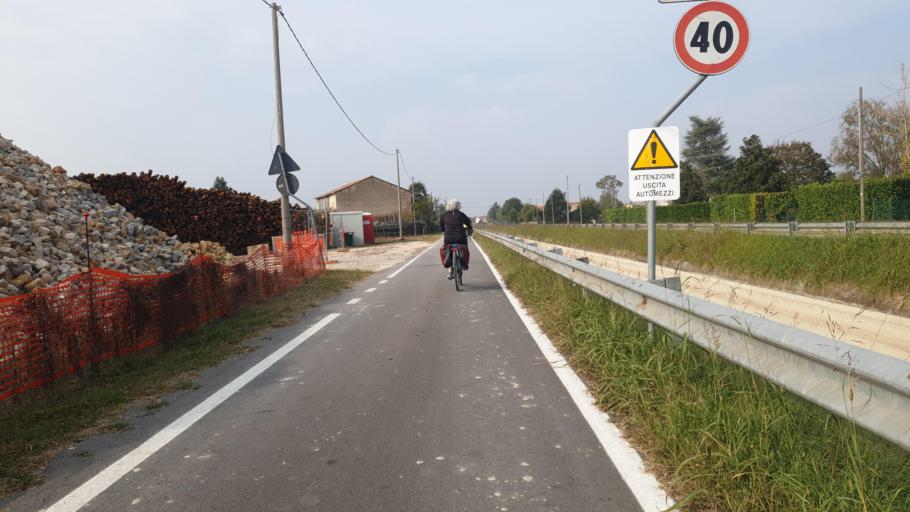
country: IT
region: Veneto
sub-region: Provincia di Padova
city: Corte
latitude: 45.3031
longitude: 12.0766
